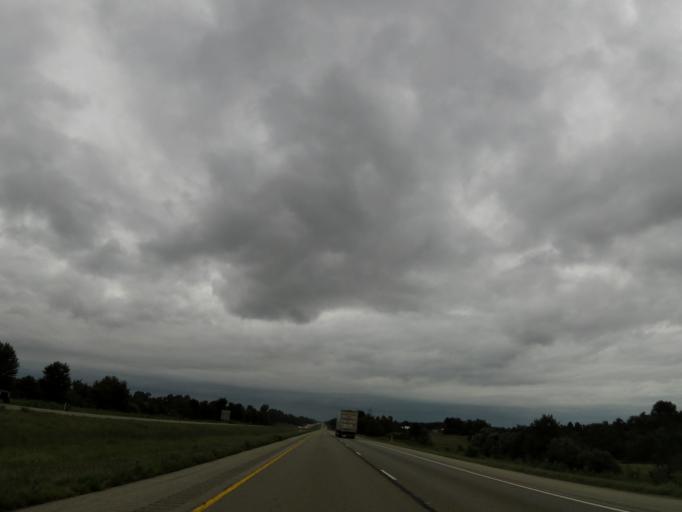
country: US
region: Illinois
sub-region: Massac County
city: Metropolis
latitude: 37.1924
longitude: -88.6862
